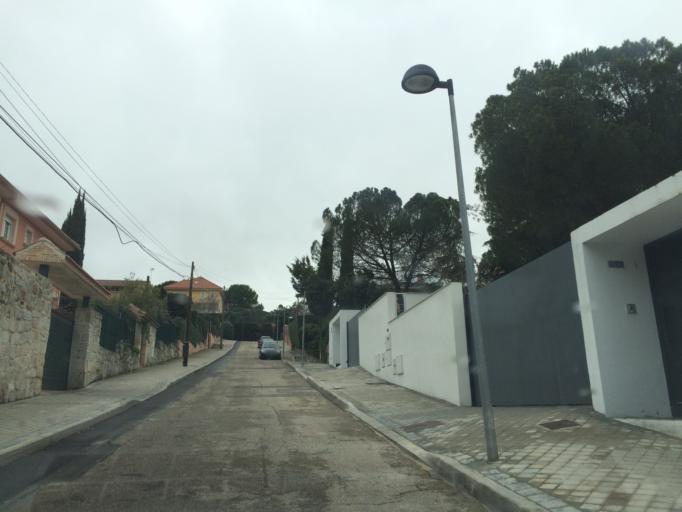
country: ES
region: Madrid
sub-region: Provincia de Madrid
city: Tres Cantos
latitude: 40.6105
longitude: -3.6874
